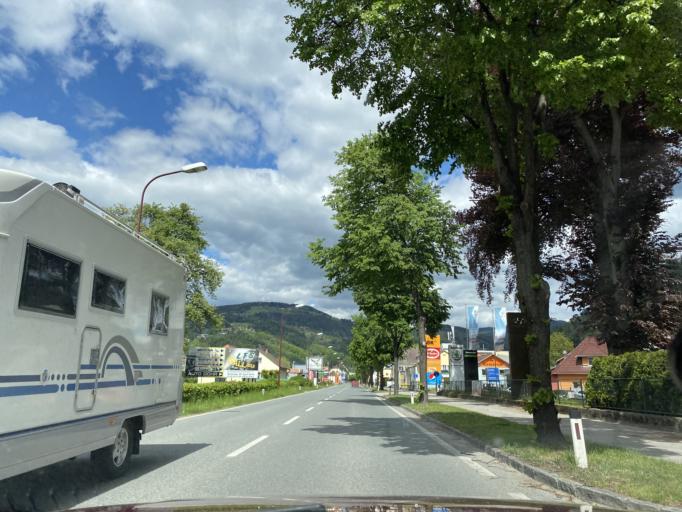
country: AT
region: Carinthia
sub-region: Politischer Bezirk Wolfsberg
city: Wolfsberg
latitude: 46.8443
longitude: 14.8429
